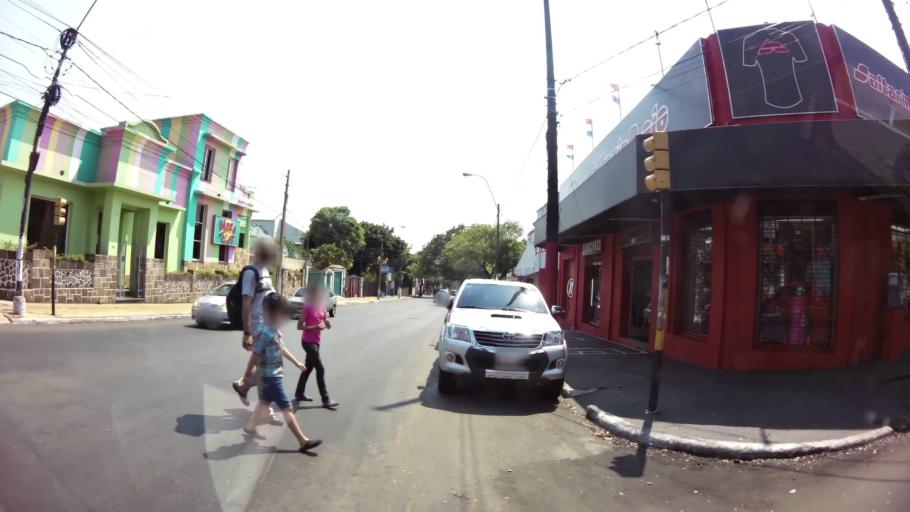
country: PY
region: Asuncion
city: Asuncion
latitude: -25.2864
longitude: -57.6470
